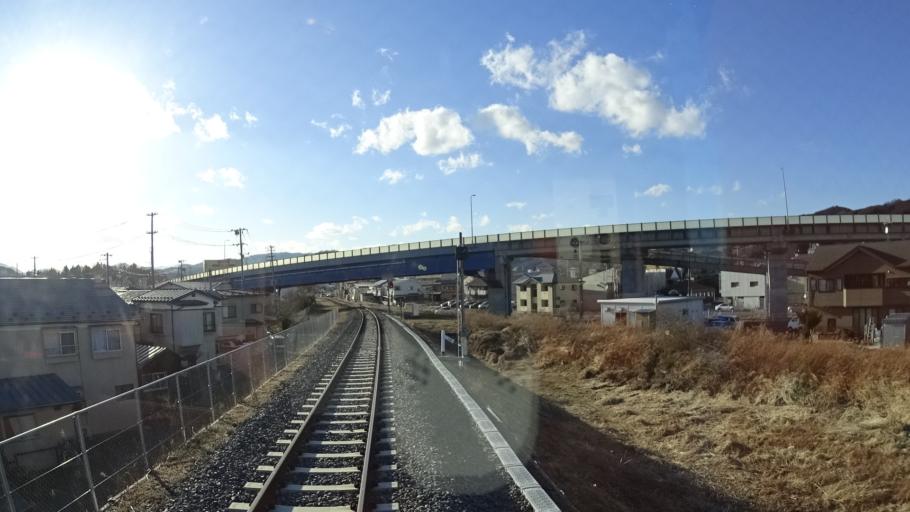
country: JP
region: Iwate
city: Miyako
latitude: 39.6387
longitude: 141.9528
